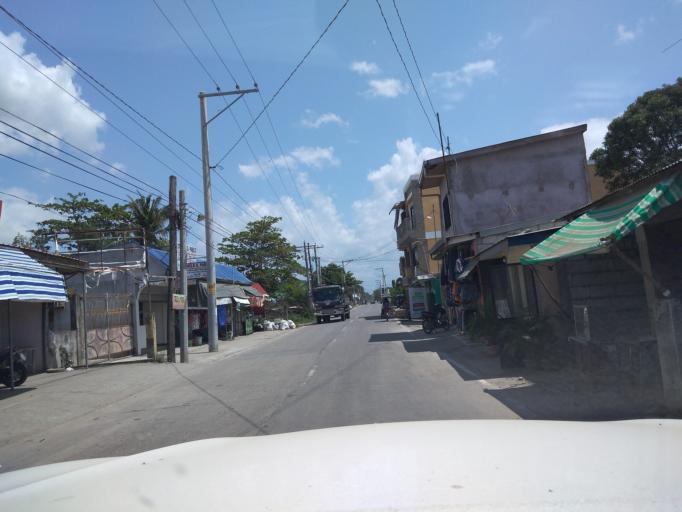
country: PH
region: Central Luzon
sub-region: Province of Pampanga
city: Lourdes
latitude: 15.0193
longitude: 120.8640
